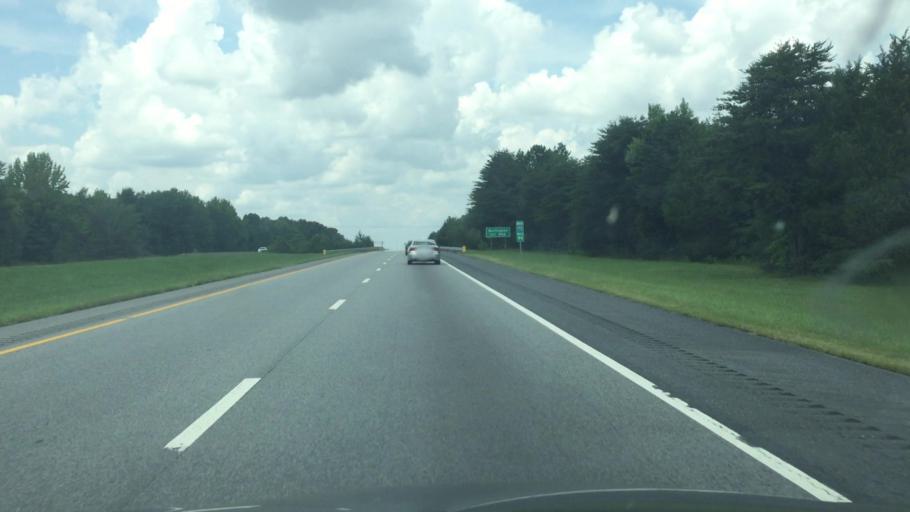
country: US
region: North Carolina
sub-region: Guilford County
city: Pleasant Garden
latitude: 35.9856
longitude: -79.8246
